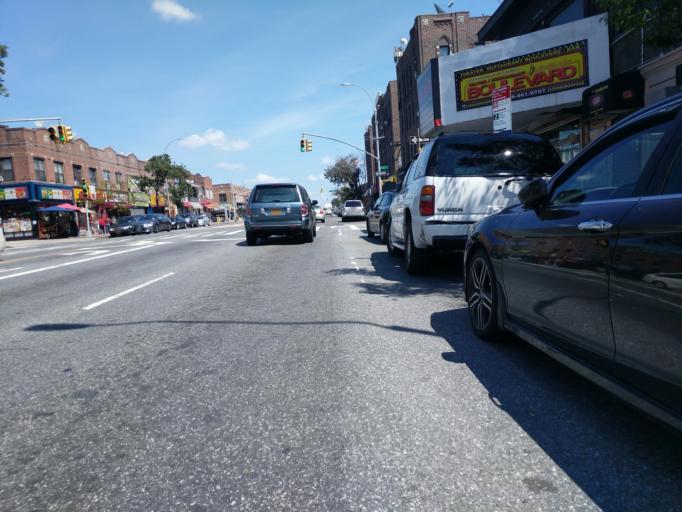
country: US
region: New York
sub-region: Queens County
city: Long Island City
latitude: 40.7555
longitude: -73.8848
